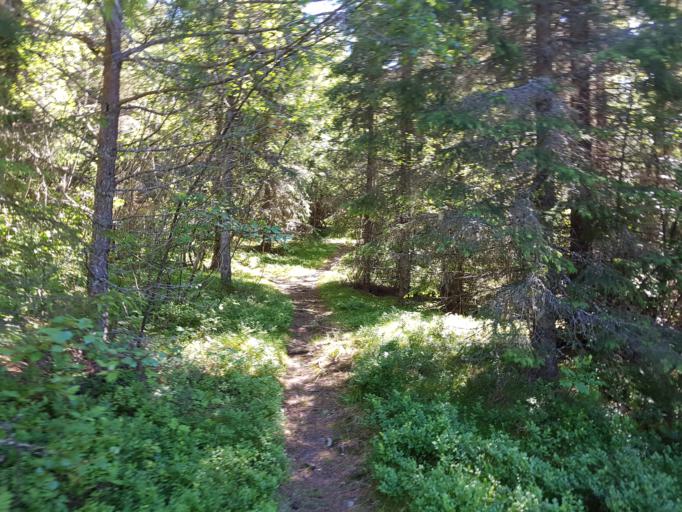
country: NO
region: Sor-Trondelag
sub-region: Skaun
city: Borsa
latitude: 63.4320
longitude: 10.1936
